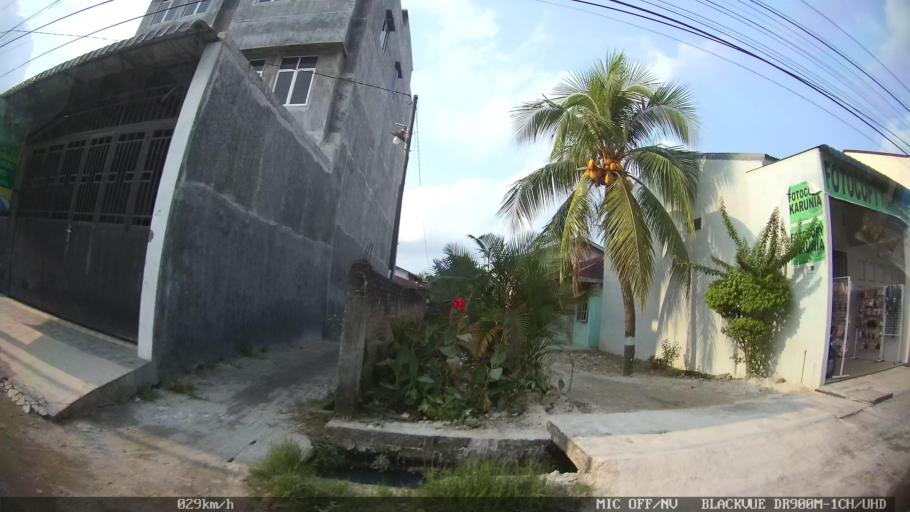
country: ID
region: North Sumatra
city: Medan
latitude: 3.5853
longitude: 98.7497
